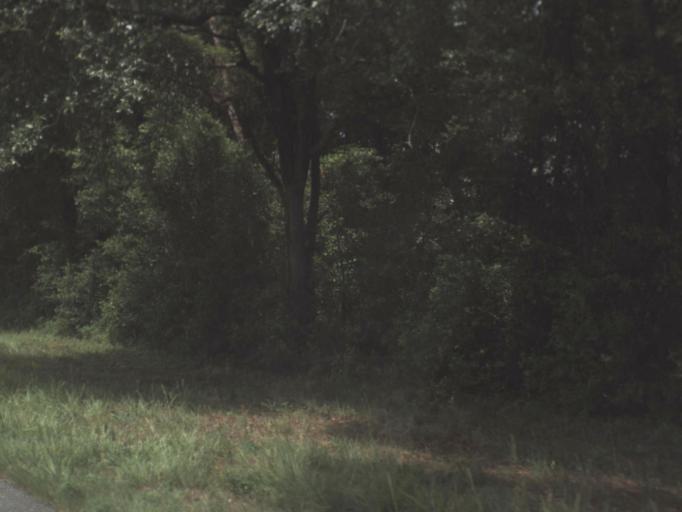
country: US
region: Florida
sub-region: Madison County
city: Madison
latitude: 30.5468
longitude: -83.3675
